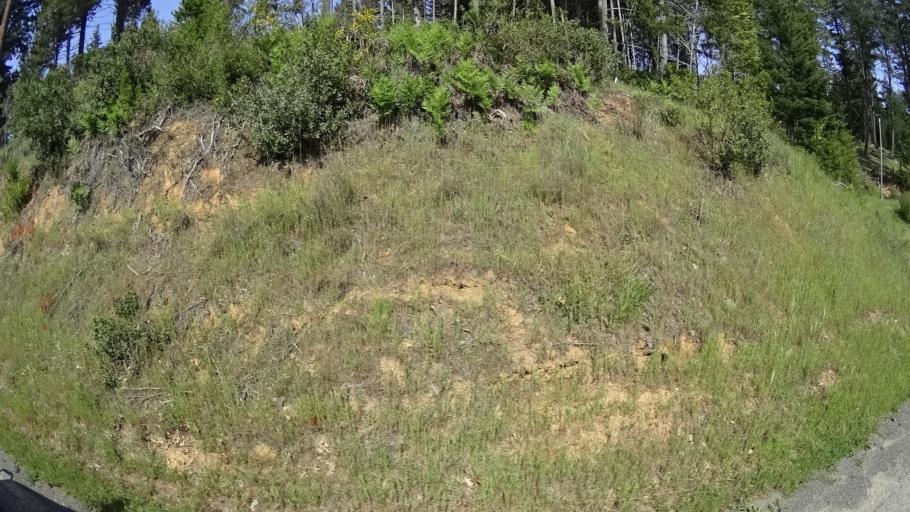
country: US
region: California
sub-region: Humboldt County
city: Redway
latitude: 40.3697
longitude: -123.7350
